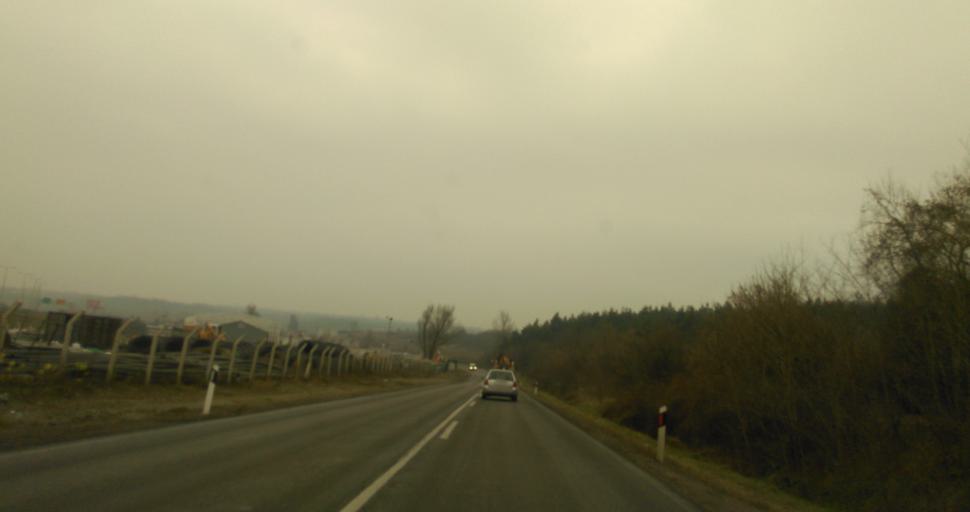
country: RS
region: Central Serbia
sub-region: Belgrade
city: Zvezdara
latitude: 44.7297
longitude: 20.5382
